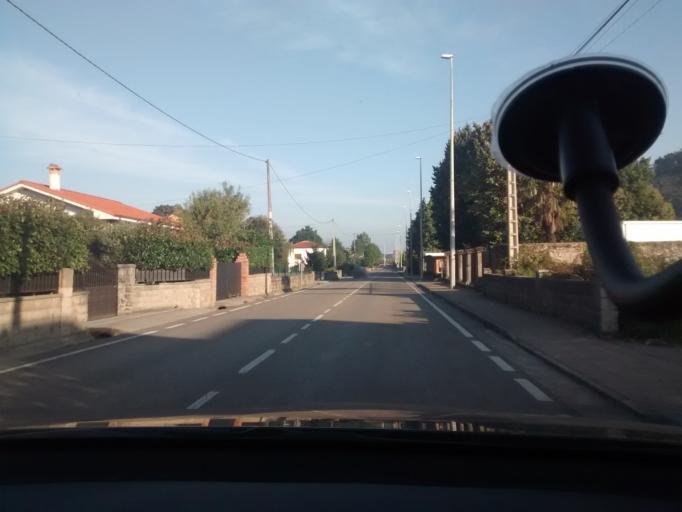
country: ES
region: Cantabria
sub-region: Provincia de Cantabria
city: Entrambasaguas
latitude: 43.3750
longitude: -3.7190
